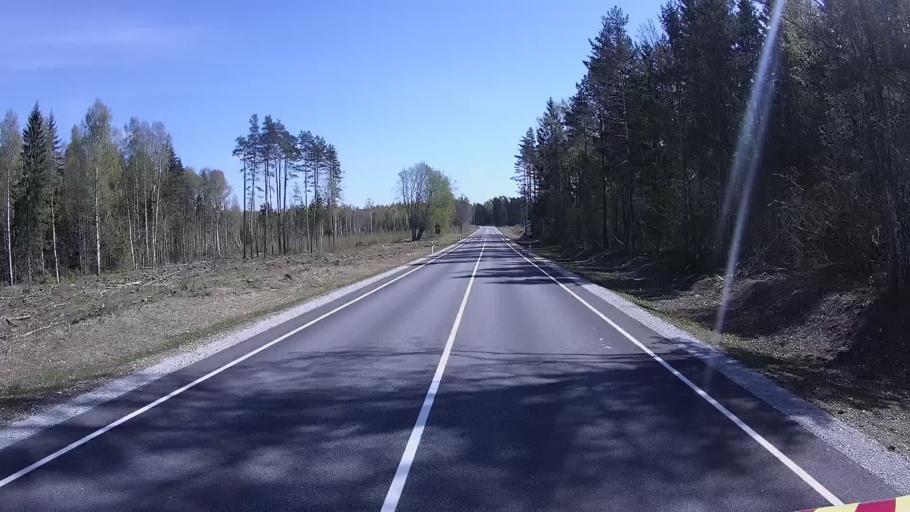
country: EE
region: Laeaene
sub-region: Ridala Parish
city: Uuemoisa
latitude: 59.0414
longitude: 23.8366
